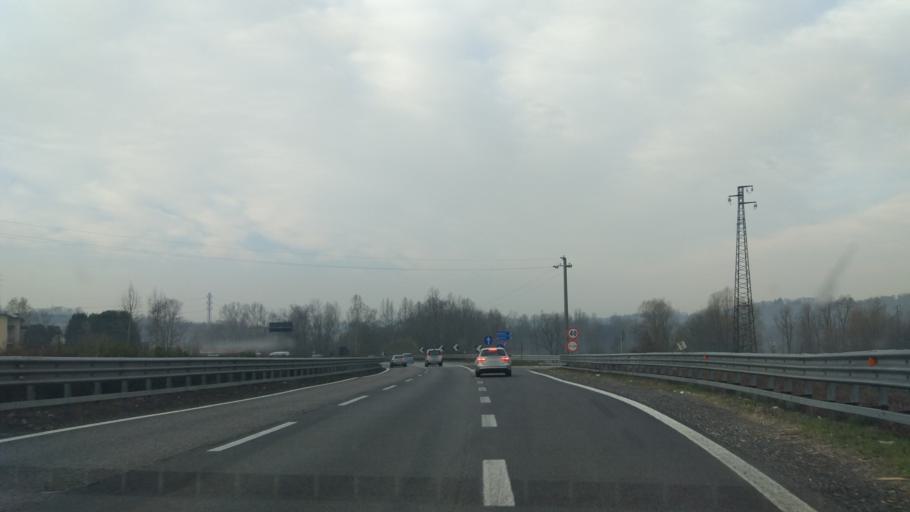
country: IT
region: Lombardy
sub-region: Provincia di Monza e Brianza
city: Capriano
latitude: 45.7379
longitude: 9.2510
